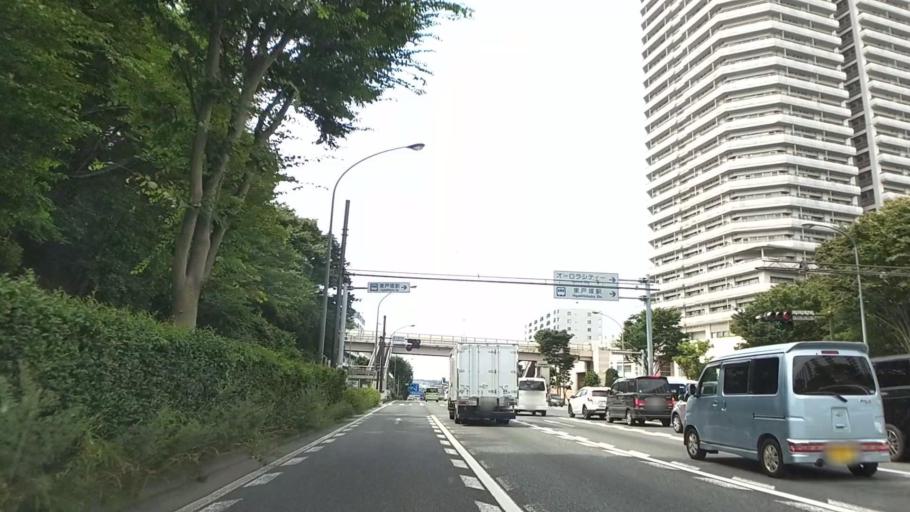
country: JP
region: Kanagawa
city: Yokohama
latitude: 35.4311
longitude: 139.5627
